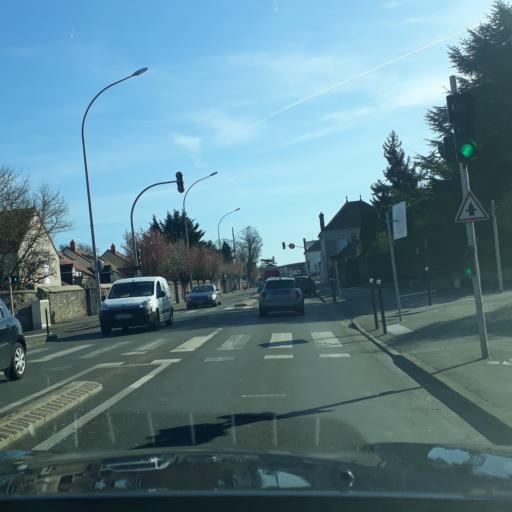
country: FR
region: Ile-de-France
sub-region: Departement de l'Essonne
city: Mennecy
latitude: 48.5630
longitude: 2.4311
